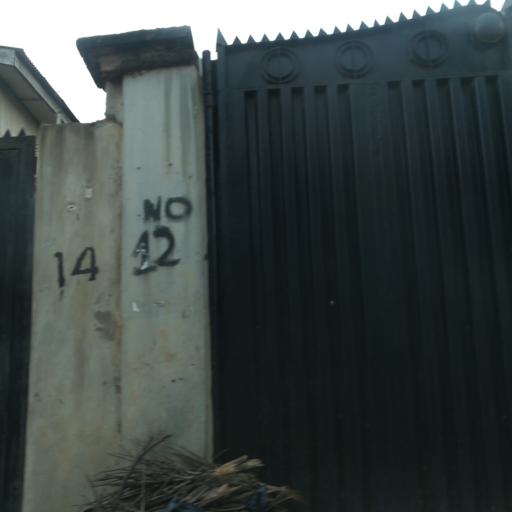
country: NG
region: Lagos
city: Agege
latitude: 6.5967
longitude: 3.2940
